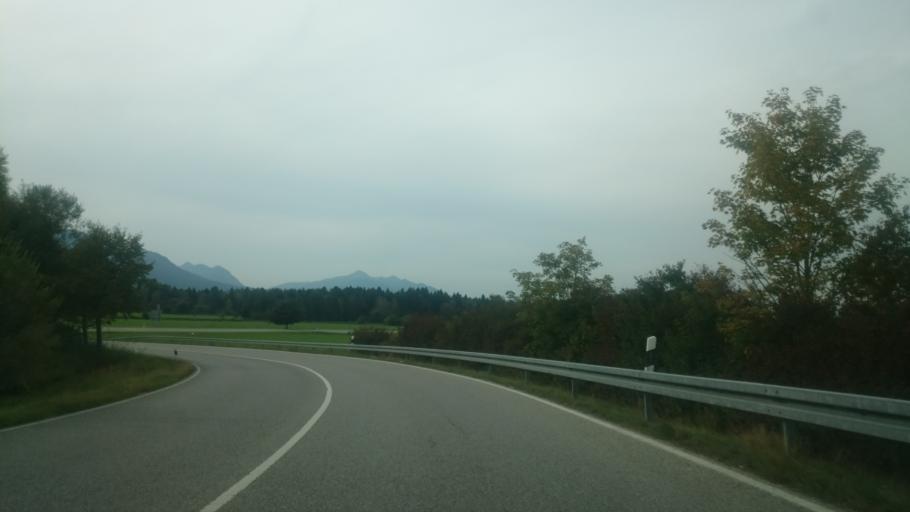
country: DE
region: Bavaria
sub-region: Swabia
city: Fuessen
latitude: 47.5804
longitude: 10.6784
